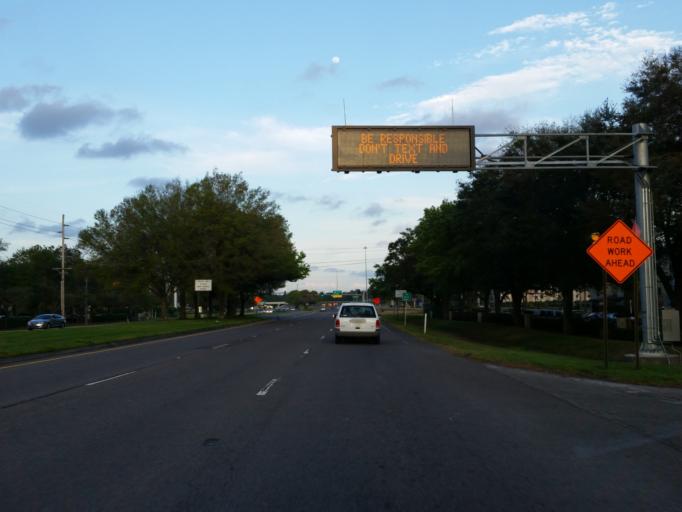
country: US
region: Florida
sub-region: Hillsborough County
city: Temple Terrace
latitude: 28.0691
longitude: -82.3624
